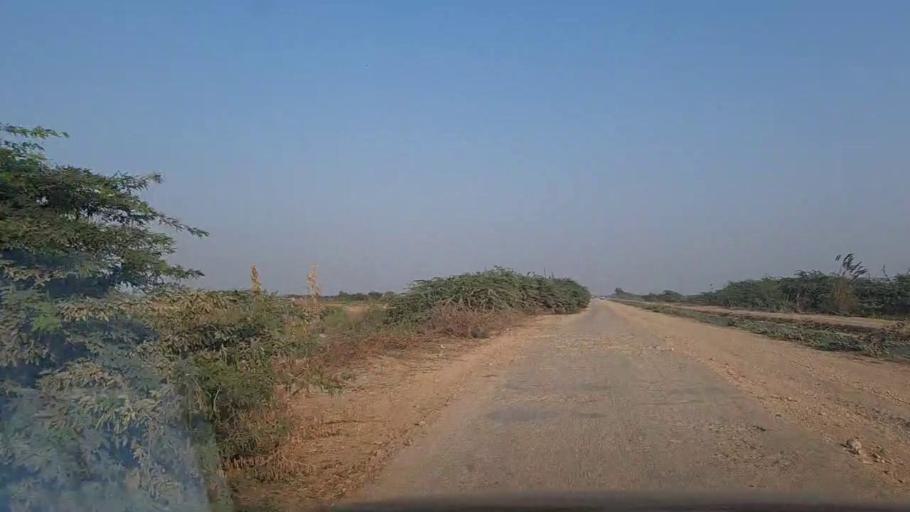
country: PK
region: Sindh
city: Keti Bandar
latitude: 24.2650
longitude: 67.5490
